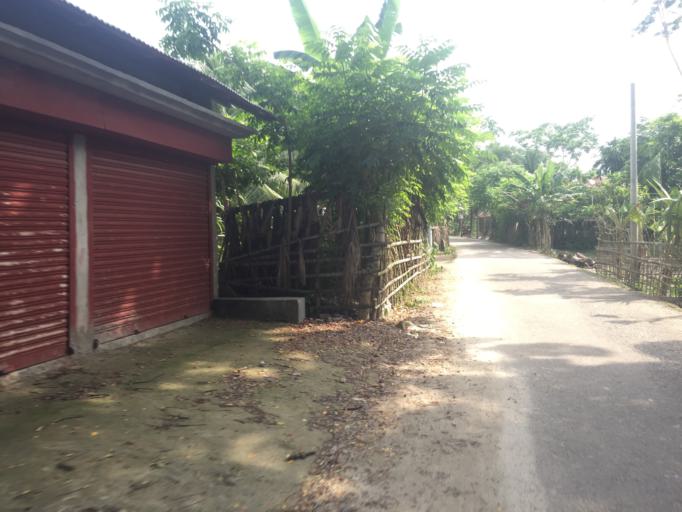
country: BD
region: Barisal
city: Mathba
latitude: 22.2600
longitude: 89.9115
